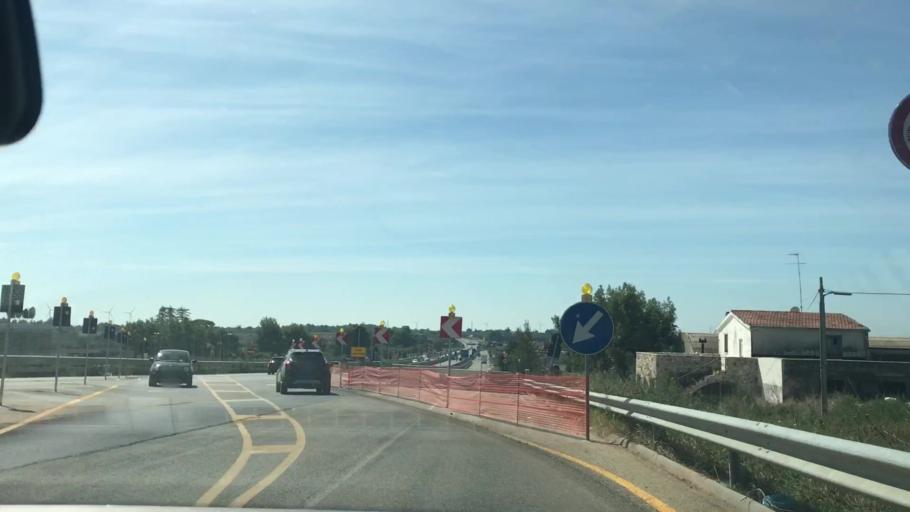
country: IT
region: Apulia
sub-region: Provincia di Bari
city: Altamura
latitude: 40.8069
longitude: 16.5555
